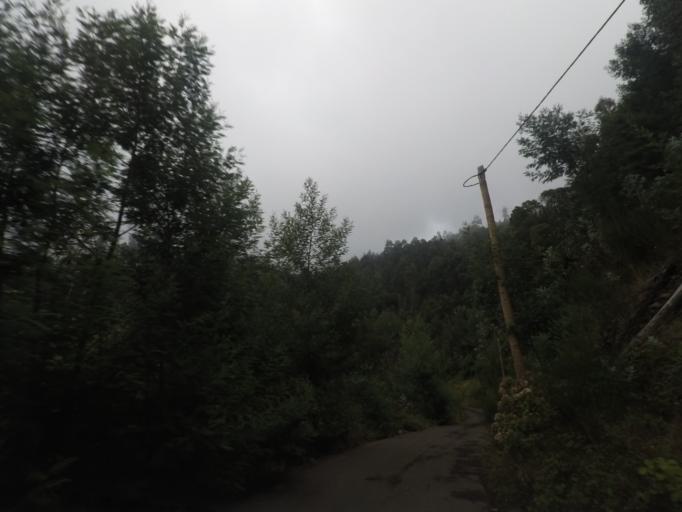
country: PT
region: Madeira
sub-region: Funchal
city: Nossa Senhora do Monte
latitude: 32.6941
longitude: -16.9081
